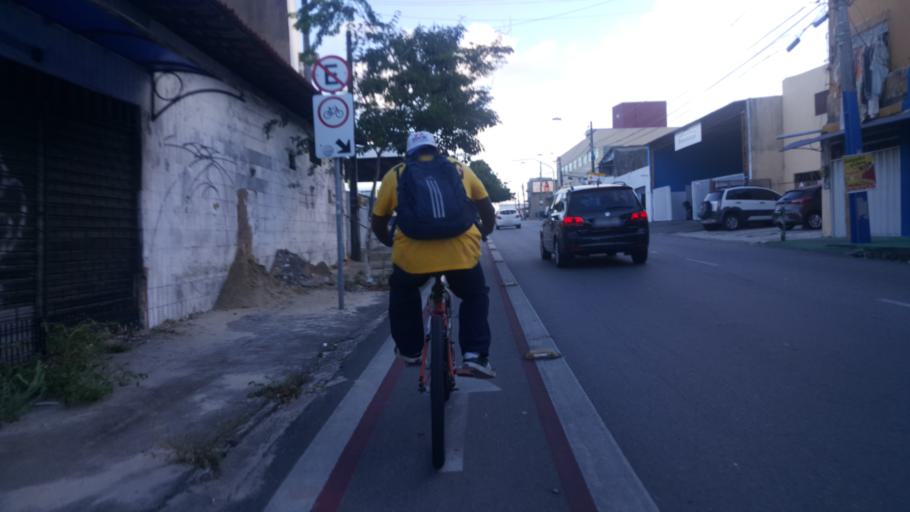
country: BR
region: Ceara
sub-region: Fortaleza
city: Fortaleza
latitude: -3.7555
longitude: -38.5417
